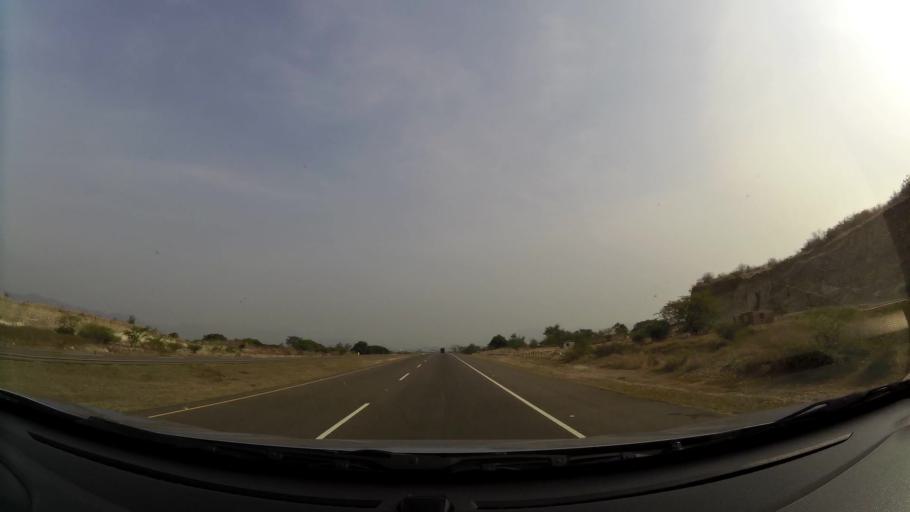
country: HN
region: Comayagua
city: Comayagua
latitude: 14.4511
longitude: -87.6635
